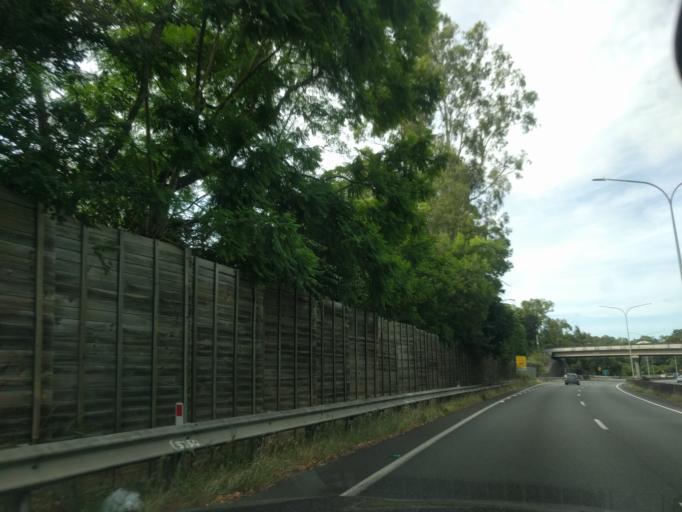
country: AU
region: Queensland
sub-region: Brisbane
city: Kenmore Hills
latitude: -27.5160
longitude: 152.9559
